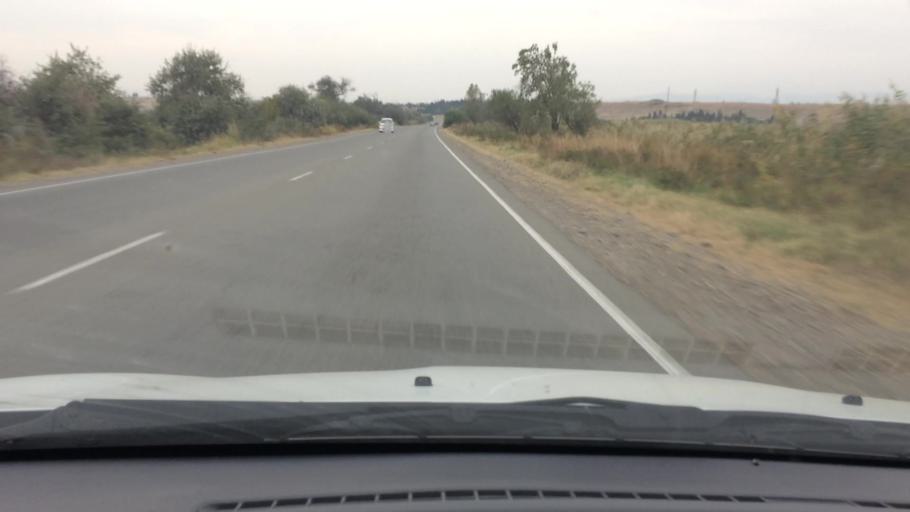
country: GE
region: Kvemo Kartli
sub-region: Marneuli
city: Marneuli
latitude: 41.5366
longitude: 44.7768
